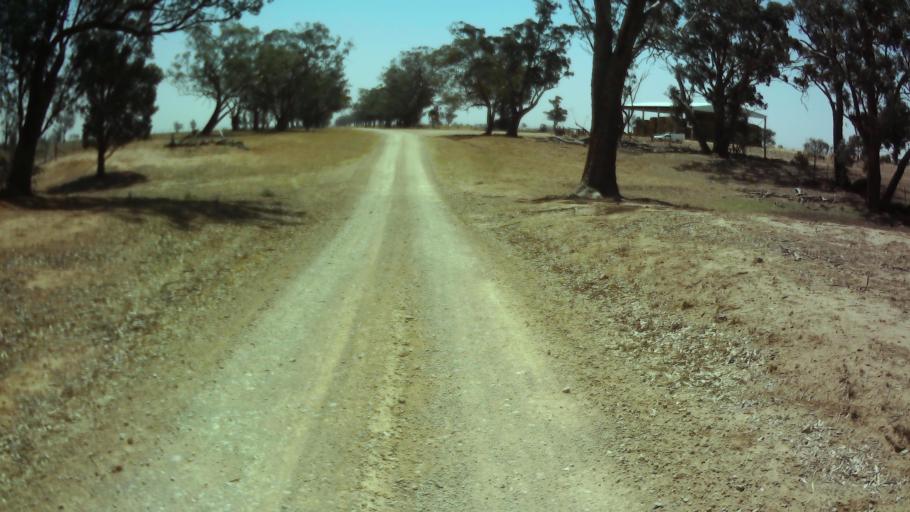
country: AU
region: New South Wales
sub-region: Weddin
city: Grenfell
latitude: -34.0138
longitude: 147.8965
